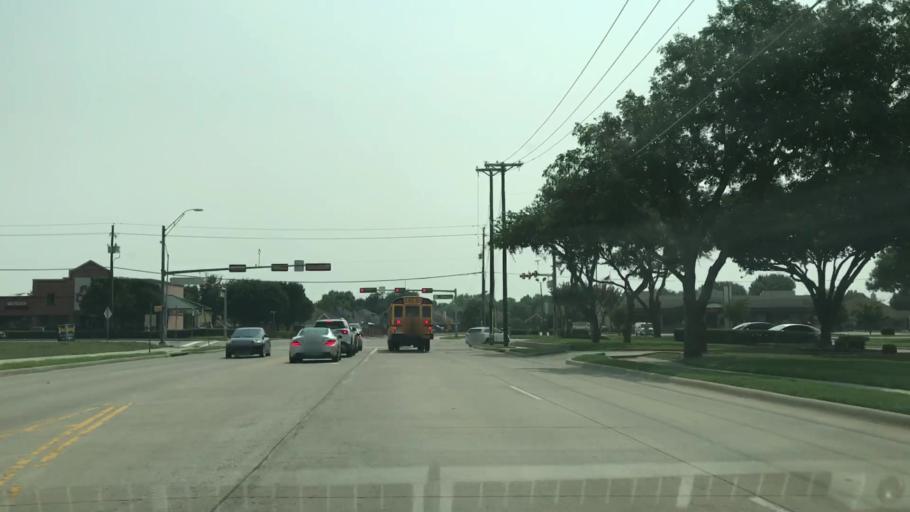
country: US
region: Texas
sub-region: Dallas County
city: Rowlett
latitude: 32.9227
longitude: -96.5782
